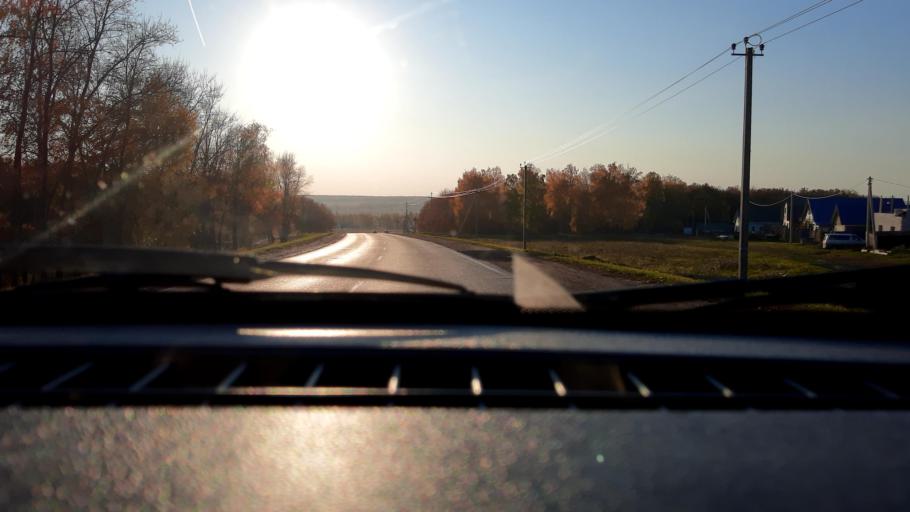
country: RU
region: Bashkortostan
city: Avdon
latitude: 54.8209
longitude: 55.7157
